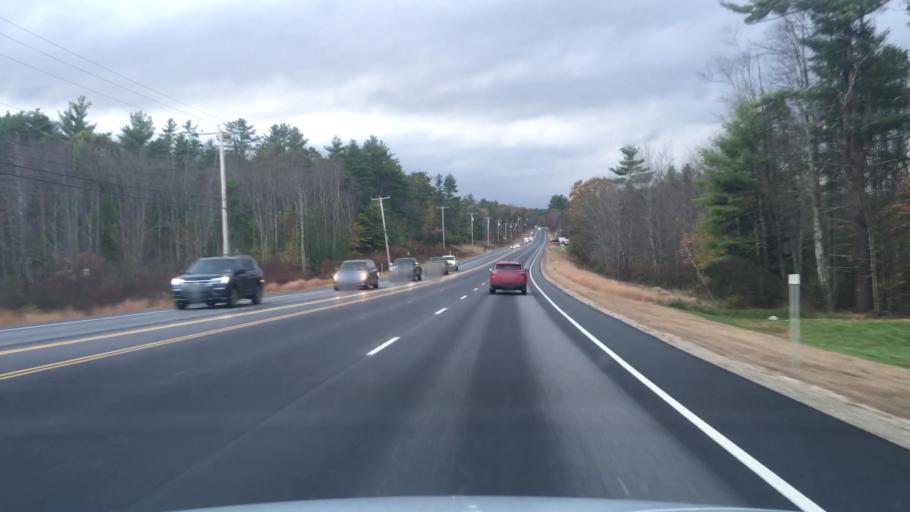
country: US
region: New Hampshire
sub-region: Merrimack County
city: Chichester
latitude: 43.2305
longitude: -71.3704
